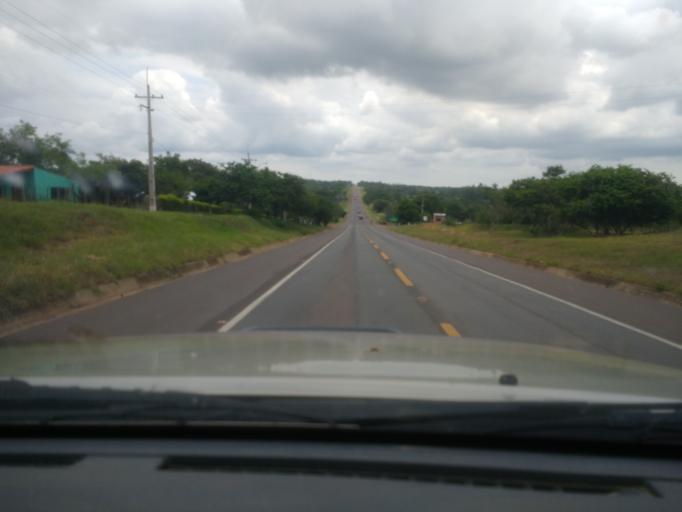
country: PY
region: Cordillera
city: Arroyos y Esteros
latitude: -25.0532
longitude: -57.1074
